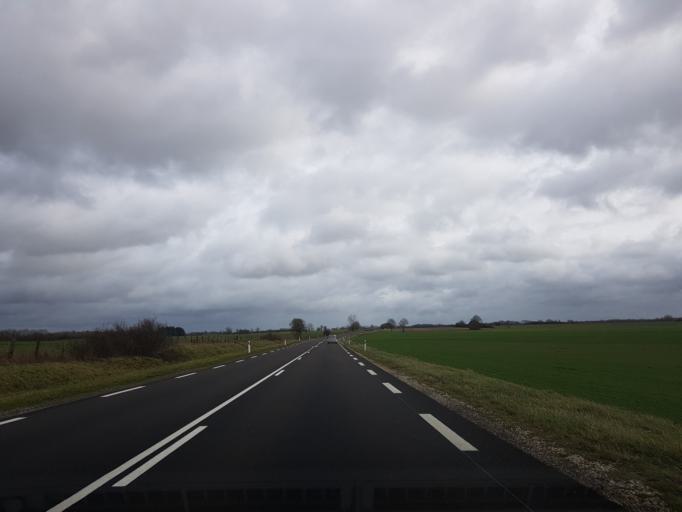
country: FR
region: Champagne-Ardenne
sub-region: Departement de la Haute-Marne
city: Chalindrey
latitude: 47.8484
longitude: 5.4233
